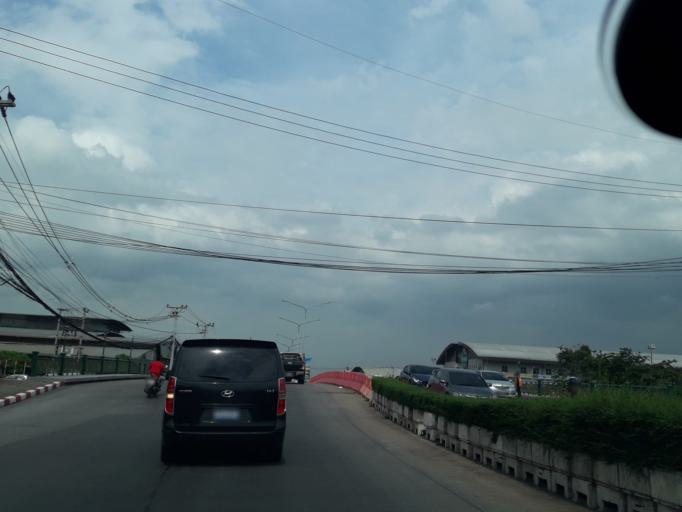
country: TH
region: Pathum Thani
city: Khlong Luang
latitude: 14.0818
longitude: 100.6196
